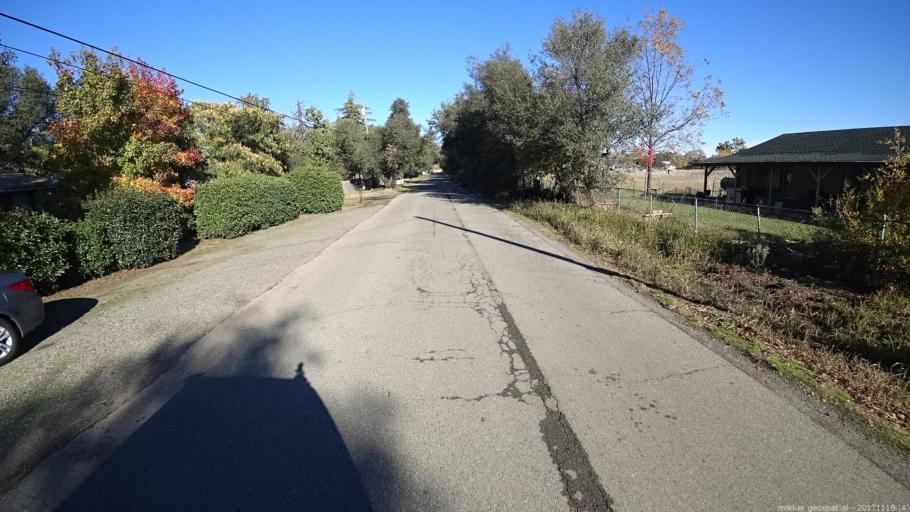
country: US
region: California
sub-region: Shasta County
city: Cottonwood
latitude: 40.3863
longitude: -122.3120
